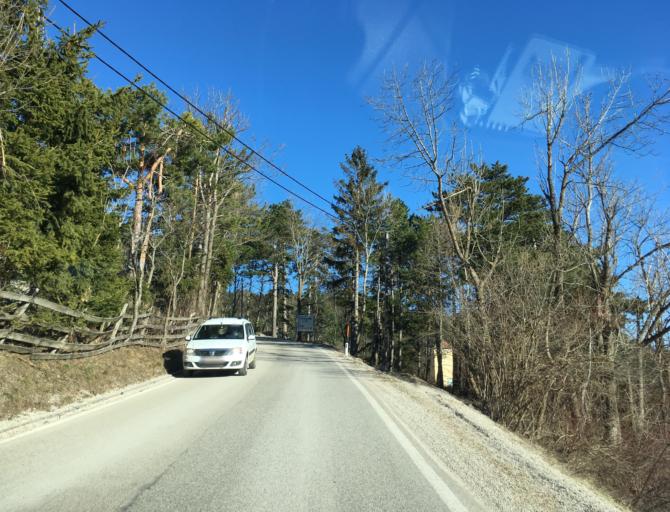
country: AT
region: Lower Austria
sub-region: Politischer Bezirk Wiener Neustadt
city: Waldegg
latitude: 47.8395
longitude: 16.0577
